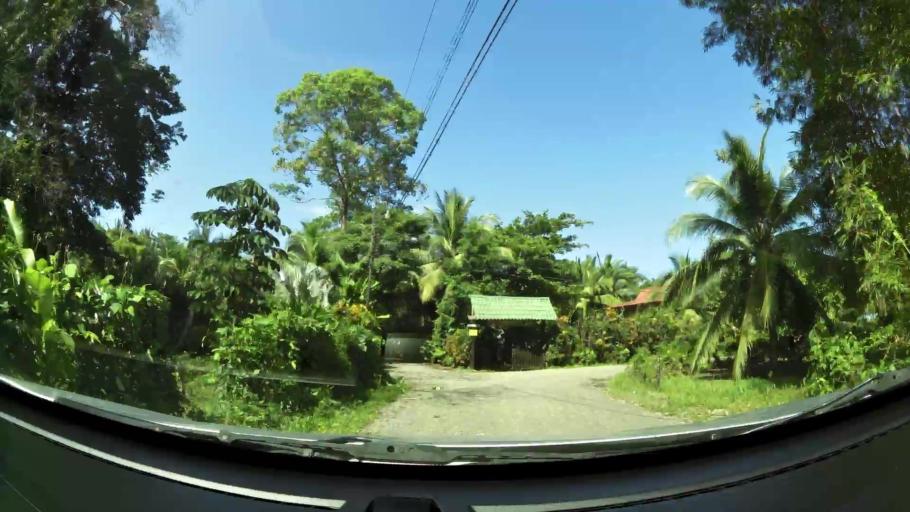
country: PA
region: Bocas del Toro
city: Barranco
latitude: 9.6400
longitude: -82.6908
